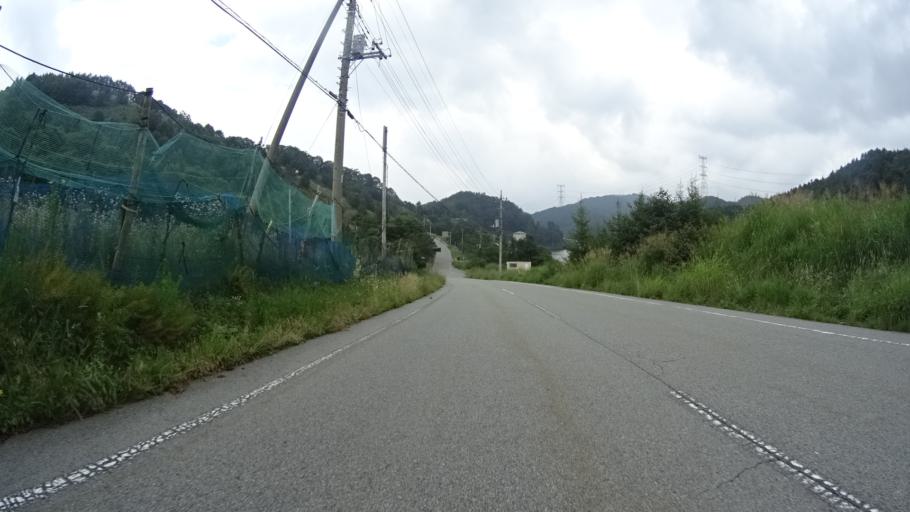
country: JP
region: Yamanashi
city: Enzan
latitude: 35.8093
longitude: 138.6555
